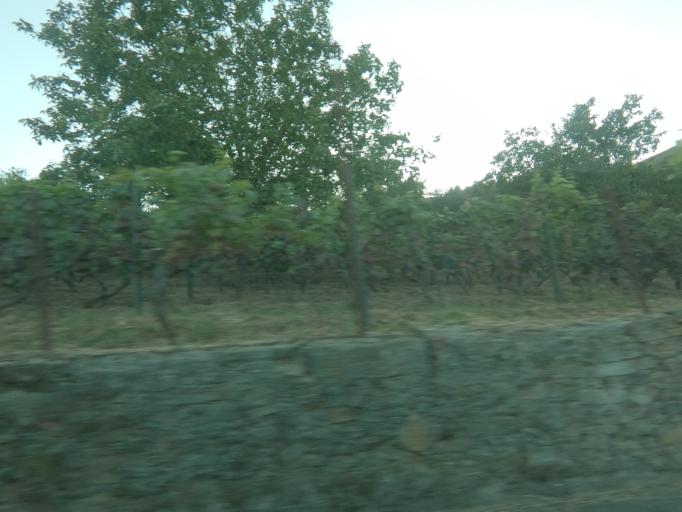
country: PT
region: Vila Real
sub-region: Mesao Frio
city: Mesao Frio
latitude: 41.1912
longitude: -7.8607
